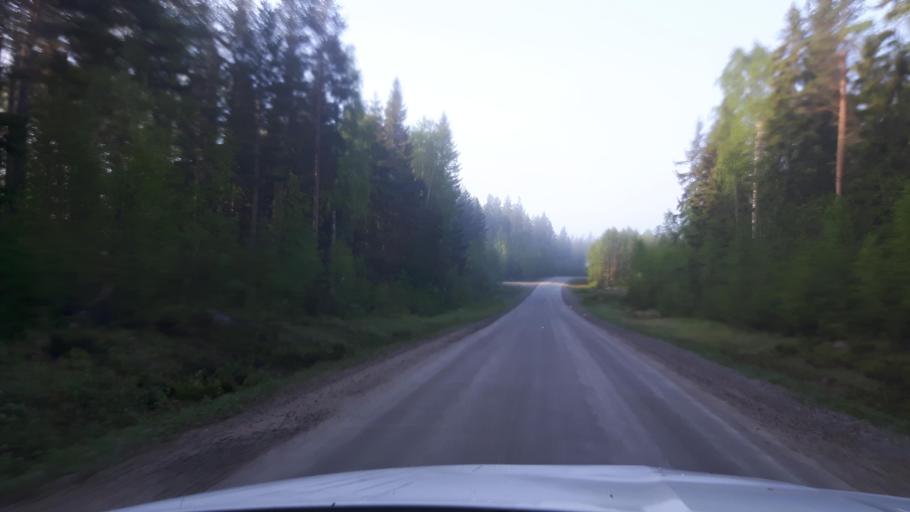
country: SE
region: Gaevleborg
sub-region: Ljusdals Kommun
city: Farila
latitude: 62.0165
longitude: 15.8379
